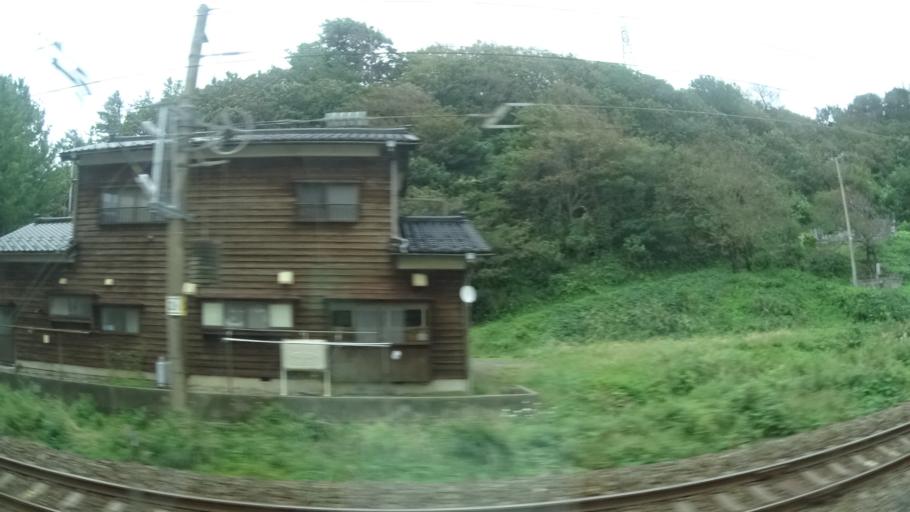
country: JP
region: Yamagata
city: Tsuruoka
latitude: 38.5508
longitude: 139.5506
